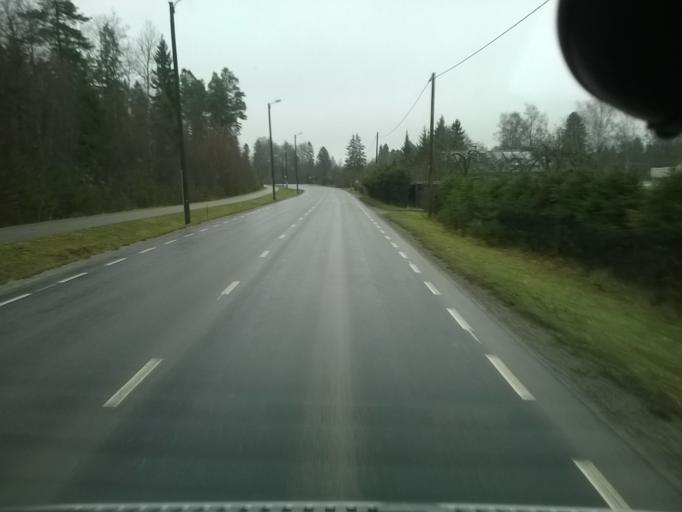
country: EE
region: Harju
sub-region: Saku vald
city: Saku
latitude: 59.2255
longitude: 24.6741
